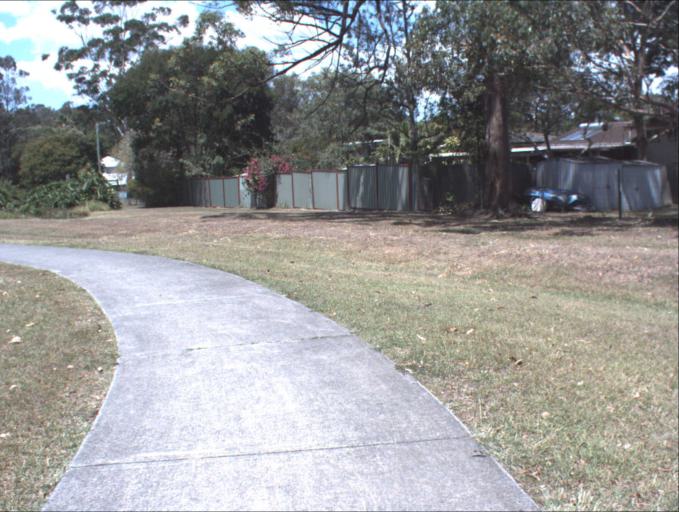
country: AU
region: Queensland
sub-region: Logan
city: Rochedale South
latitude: -27.6022
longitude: 153.1152
